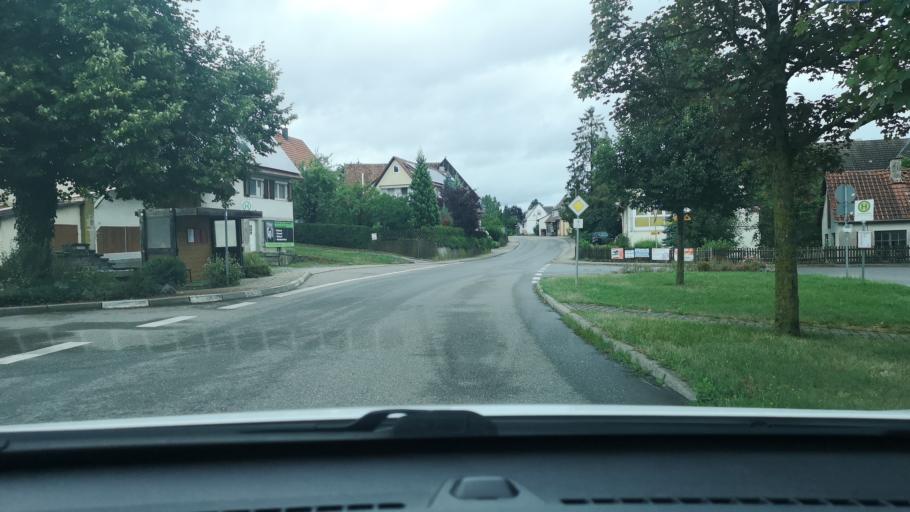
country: DE
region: Baden-Wuerttemberg
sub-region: Freiburg Region
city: Vohringen
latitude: 48.3326
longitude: 8.6568
